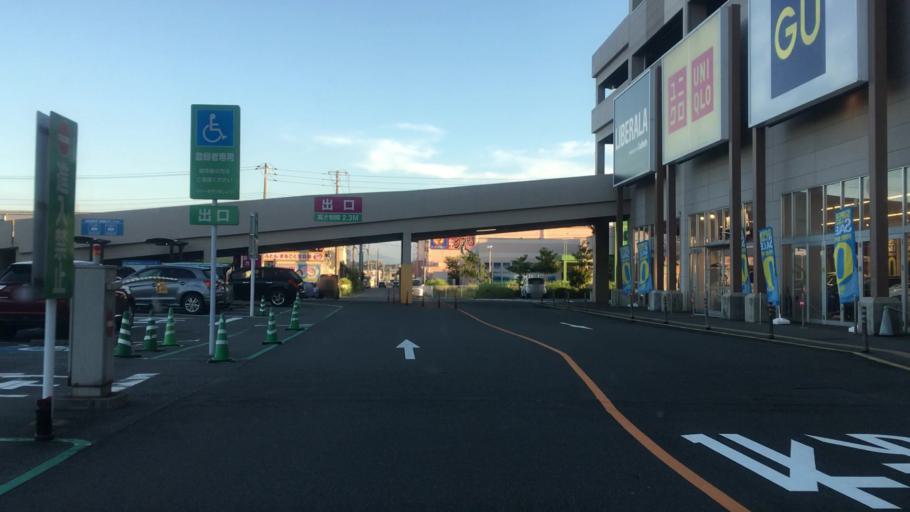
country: JP
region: Tottori
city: Tottori
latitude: 35.5232
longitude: 134.2015
